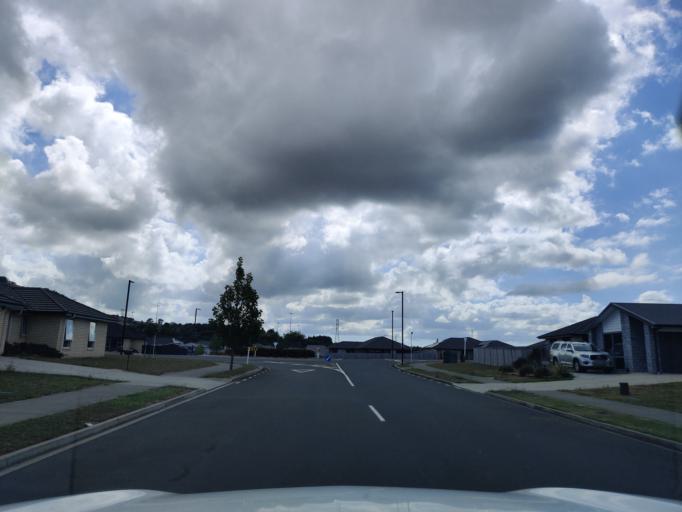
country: NZ
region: Auckland
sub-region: Auckland
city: Pukekohe East
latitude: -37.2332
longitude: 175.0127
